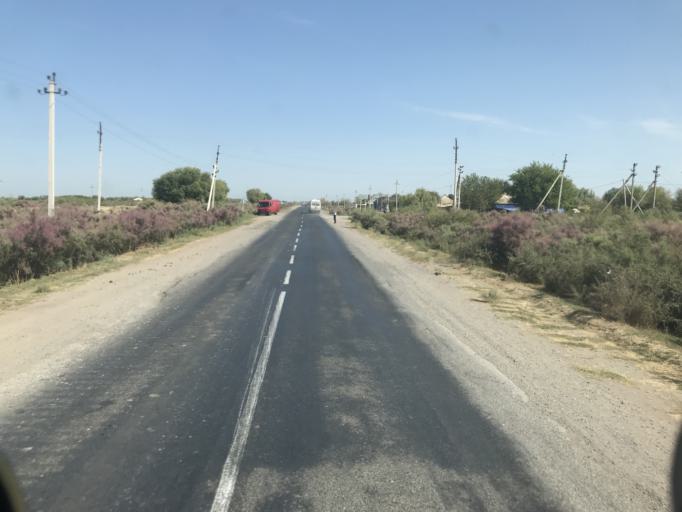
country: KZ
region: Ongtustik Qazaqstan
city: Myrzakent
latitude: 40.7289
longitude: 68.5364
